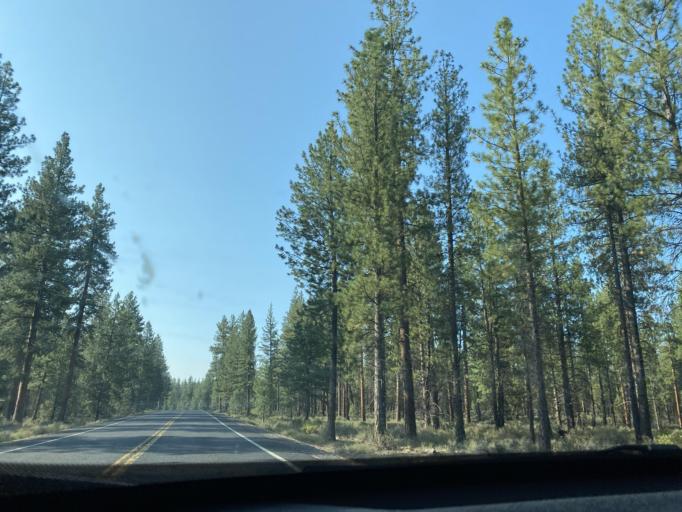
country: US
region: Oregon
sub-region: Deschutes County
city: La Pine
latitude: 43.7158
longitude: -121.4129
